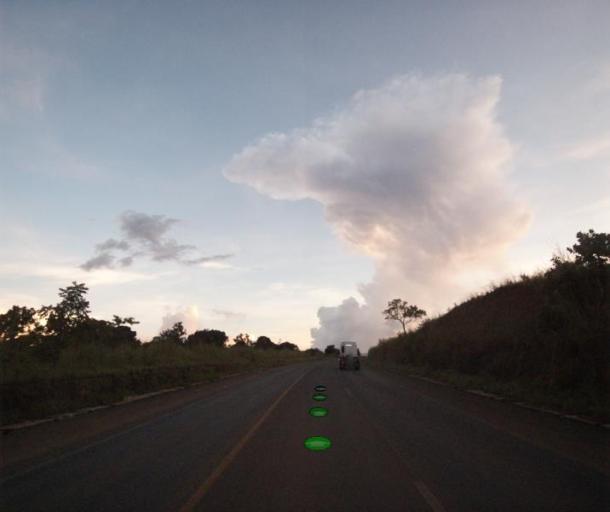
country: BR
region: Goias
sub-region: Uruacu
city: Uruacu
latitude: -14.5098
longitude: -49.1483
